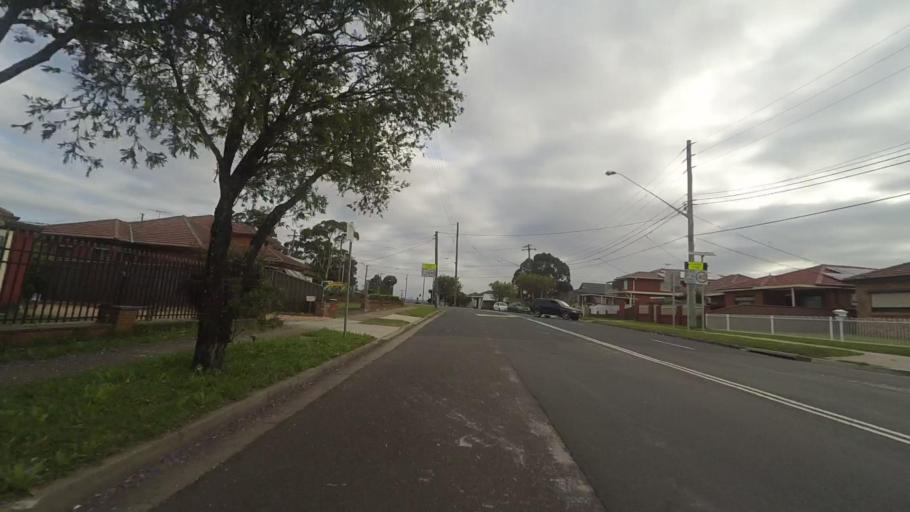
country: AU
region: New South Wales
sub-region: Bankstown
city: Bankstown
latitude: -33.9241
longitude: 151.0126
